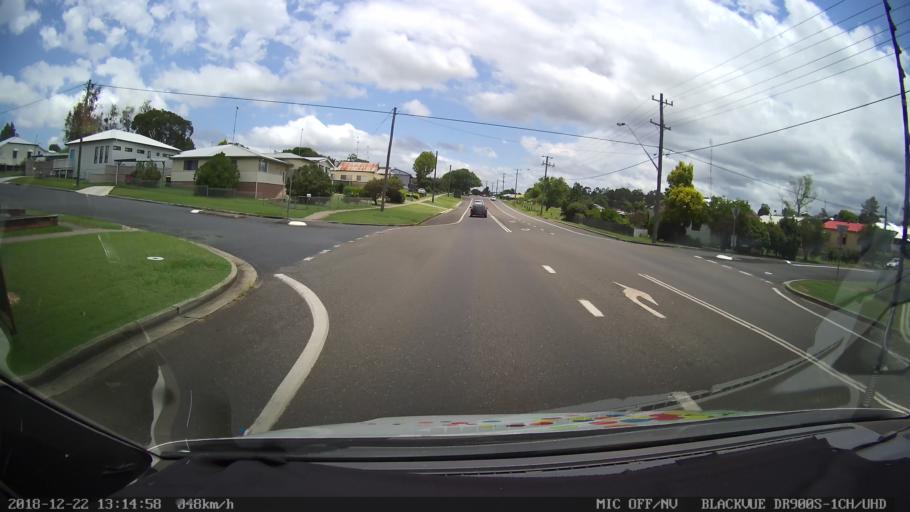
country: AU
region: New South Wales
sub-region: Clarence Valley
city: South Grafton
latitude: -29.7144
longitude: 152.9400
